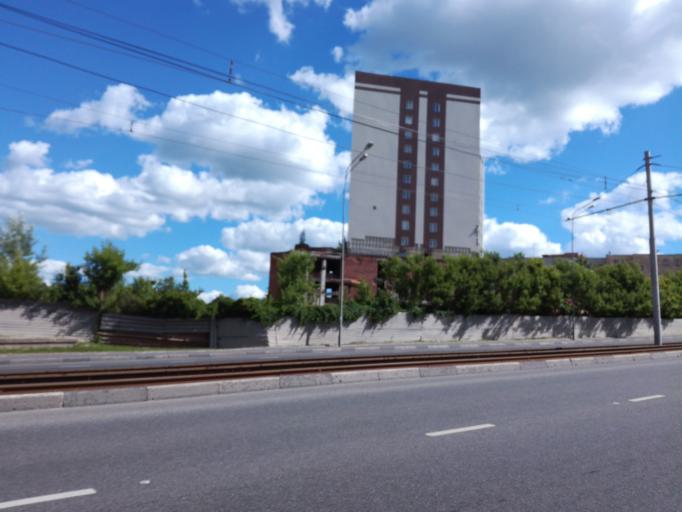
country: RU
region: Kursk
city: Kursk
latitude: 51.7540
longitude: 36.2027
